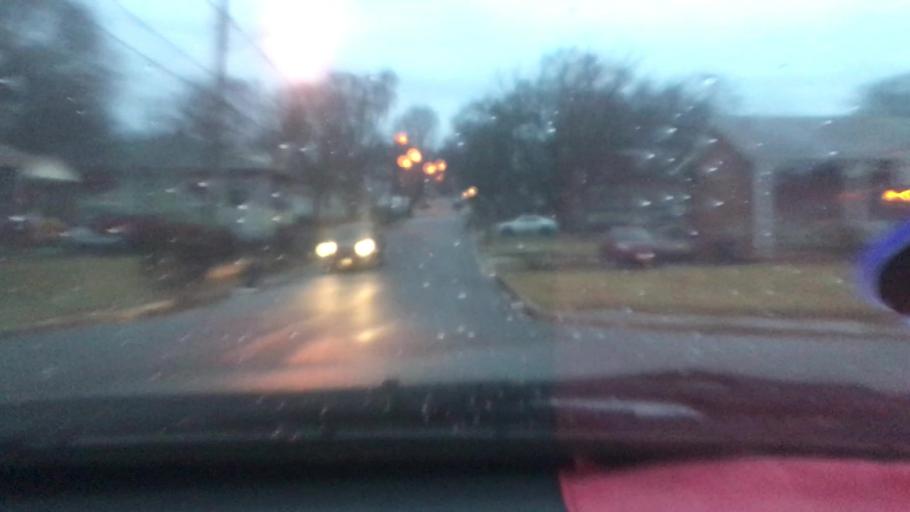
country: US
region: Maryland
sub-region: Prince George's County
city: Capitol Heights
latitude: 38.8895
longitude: -76.9099
